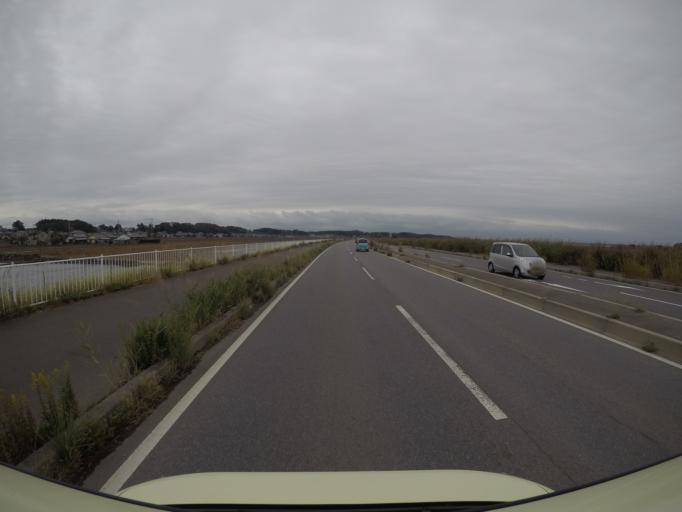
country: JP
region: Ibaraki
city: Ami
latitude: 36.0949
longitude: 140.2271
